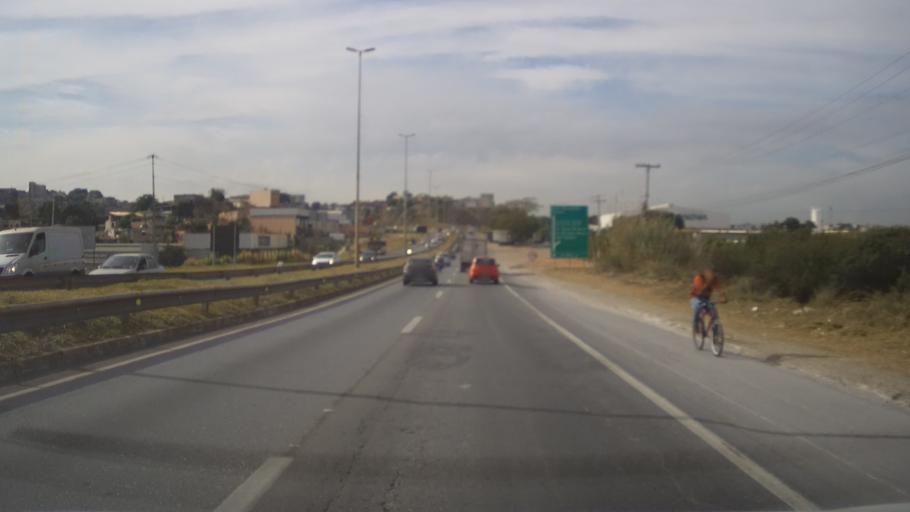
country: BR
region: Minas Gerais
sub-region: Contagem
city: Contagem
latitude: -19.9148
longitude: -44.0402
